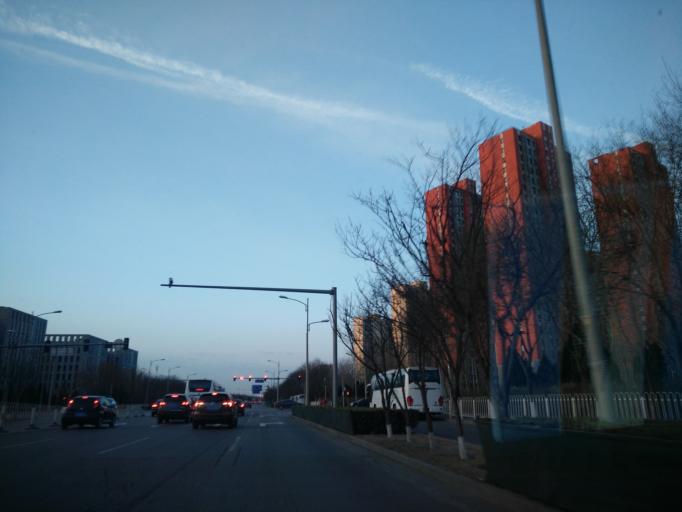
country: CN
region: Beijing
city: Jiugong
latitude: 39.7634
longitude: 116.5071
